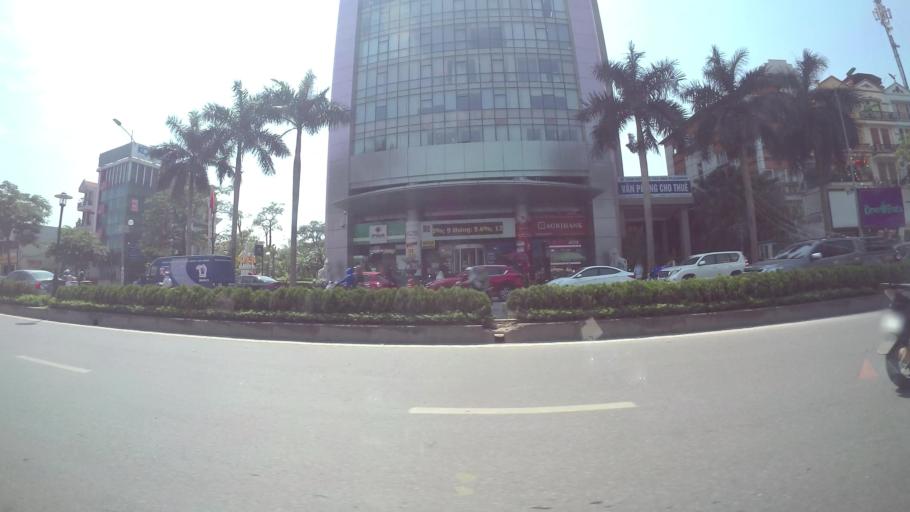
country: VN
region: Ha Noi
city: Hoan Kiem
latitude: 21.0500
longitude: 105.8836
